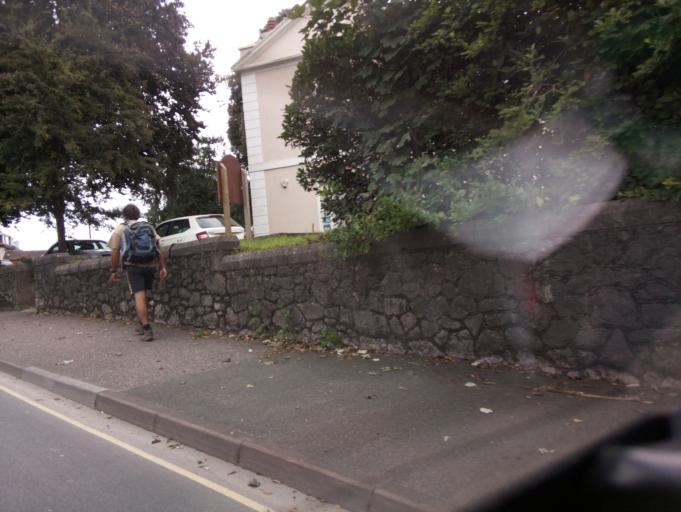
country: GB
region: England
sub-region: Devon
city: Teignmouth
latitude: 50.5478
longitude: -3.5047
